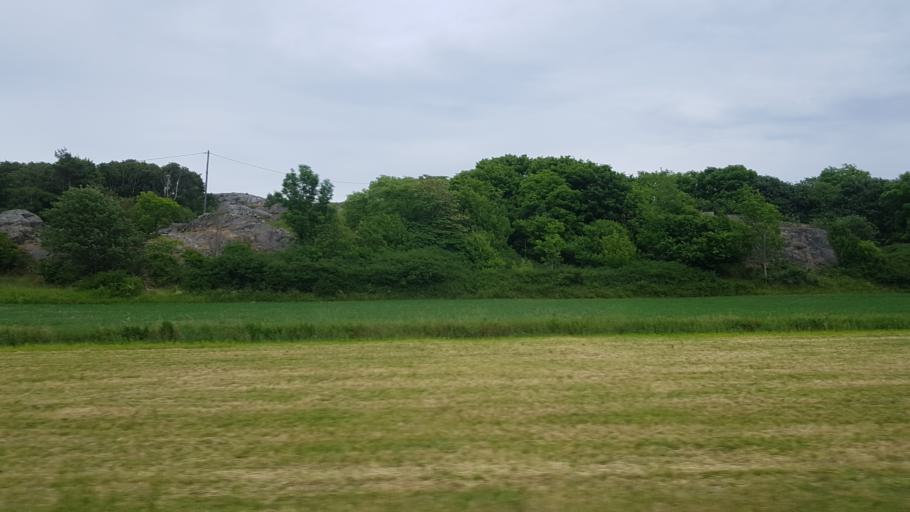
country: SE
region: Vaestra Goetaland
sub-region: Tjorns Kommun
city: Skaerhamn
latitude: 57.9695
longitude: 11.5570
